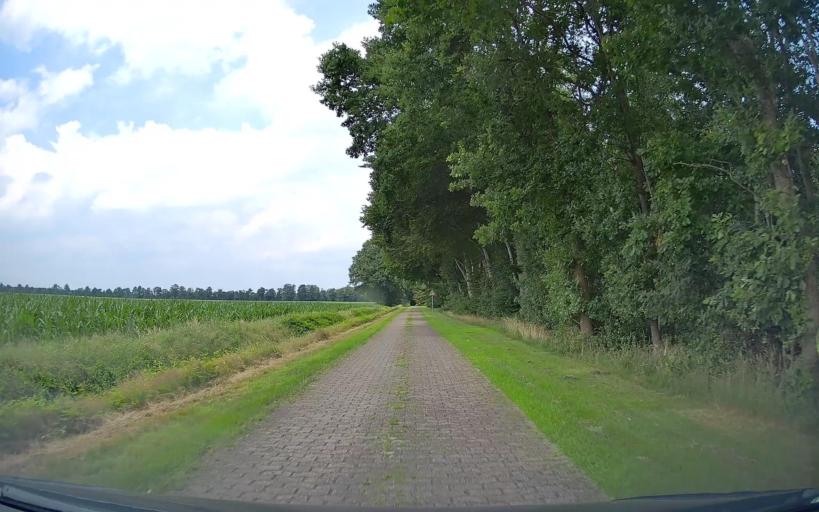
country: DE
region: Lower Saxony
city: Bosel
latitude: 52.9932
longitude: 7.9021
